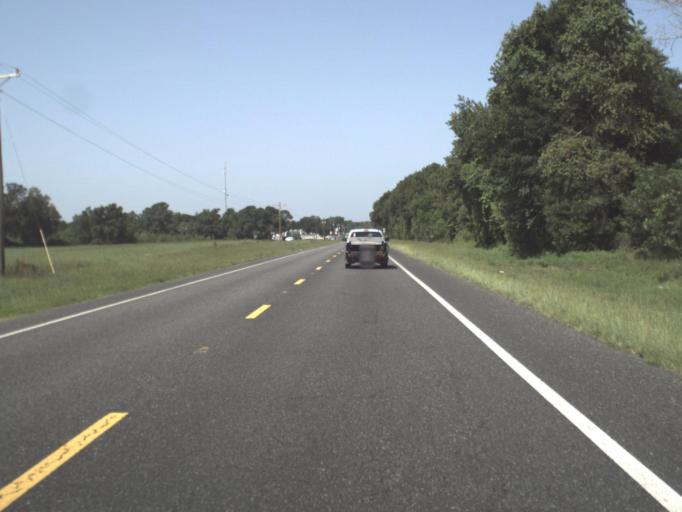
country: US
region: Florida
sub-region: Levy County
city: Chiefland
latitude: 29.4923
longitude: -82.8518
